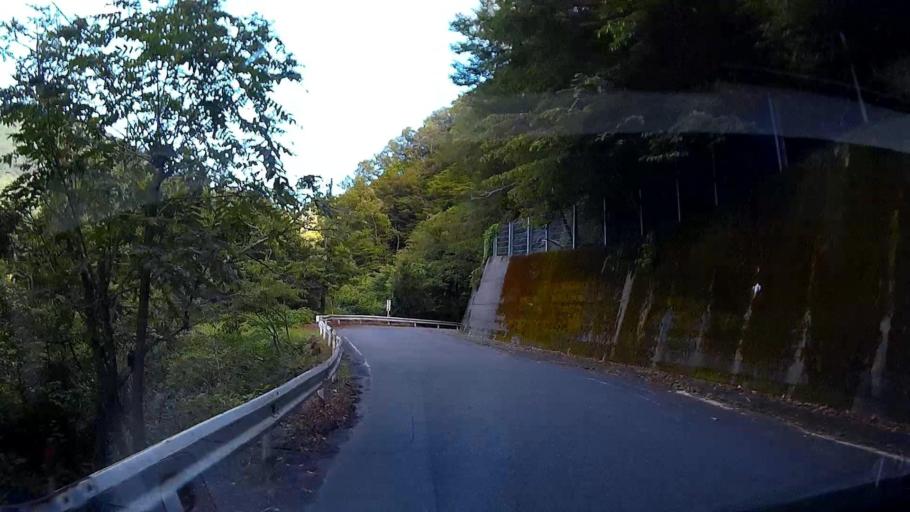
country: JP
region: Shizuoka
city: Shizuoka-shi
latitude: 35.2962
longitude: 138.2157
